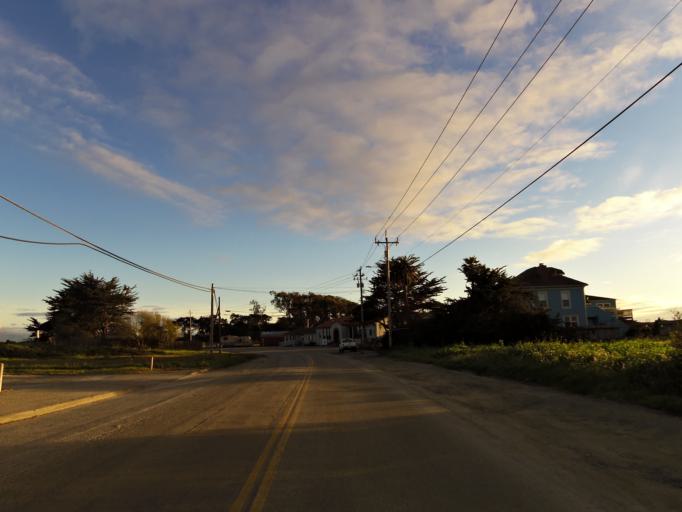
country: US
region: California
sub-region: Monterey County
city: Castroville
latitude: 36.7976
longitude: -121.7862
